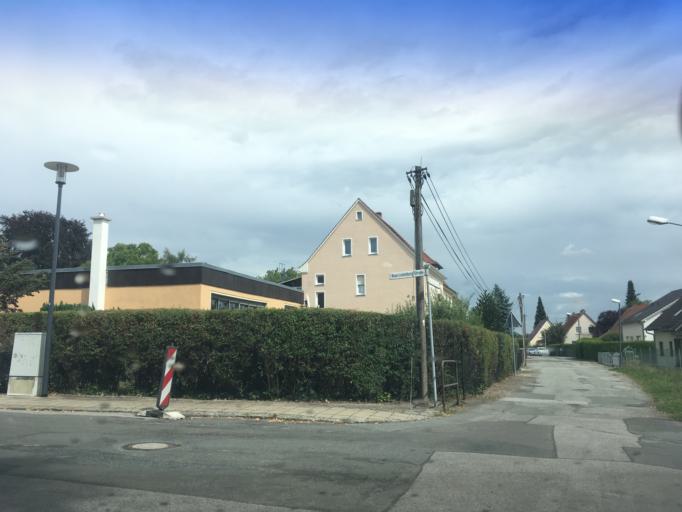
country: DE
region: Saxony
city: Goerlitz
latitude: 51.1436
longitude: 14.9508
